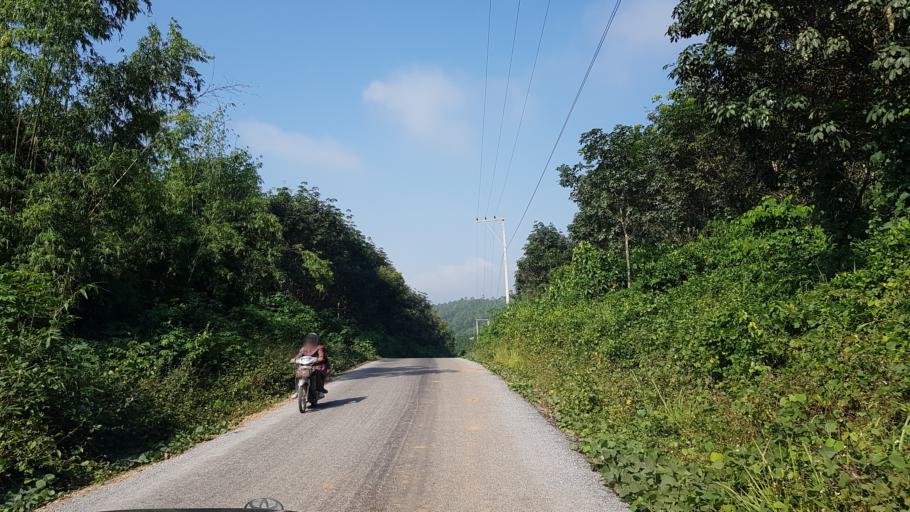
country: LA
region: Oudomxai
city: Muang Xay
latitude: 20.7131
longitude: 102.0682
